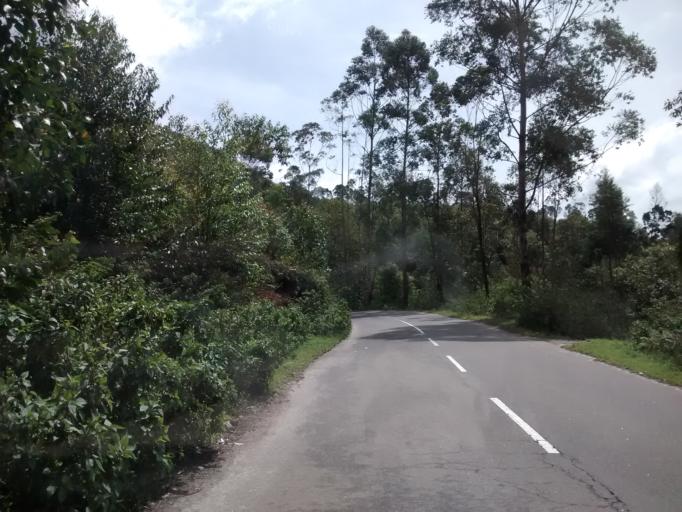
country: IN
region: Kerala
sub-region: Idukki
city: Munnar
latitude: 10.0980
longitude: 77.1024
